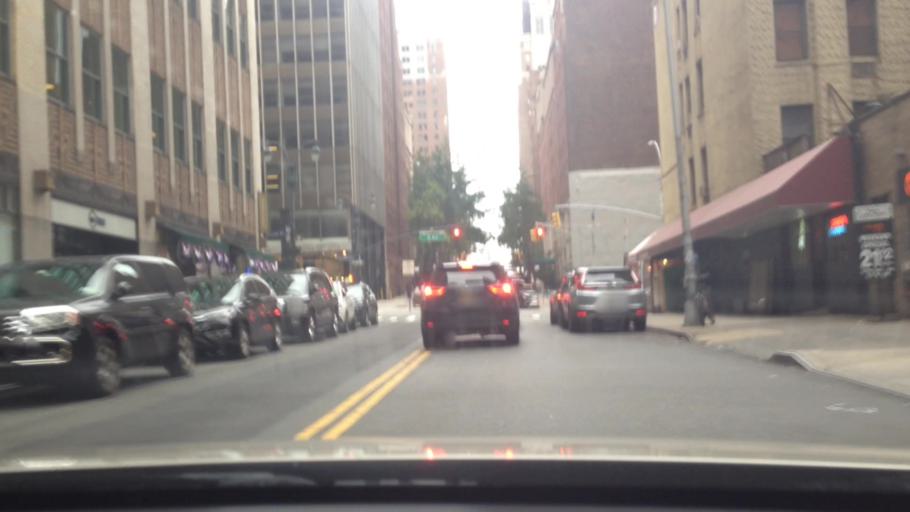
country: US
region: New York
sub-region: Queens County
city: Long Island City
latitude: 40.7500
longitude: -73.9731
